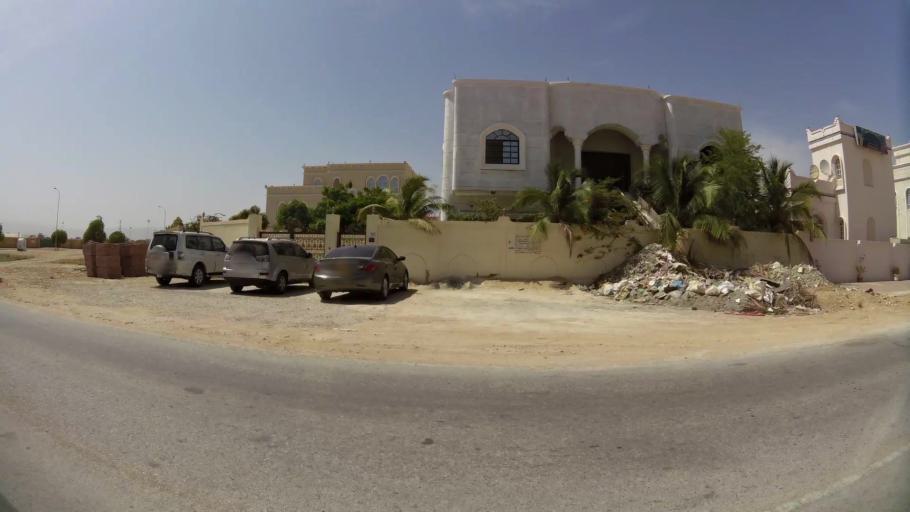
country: OM
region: Zufar
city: Salalah
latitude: 17.0388
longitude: 54.1495
